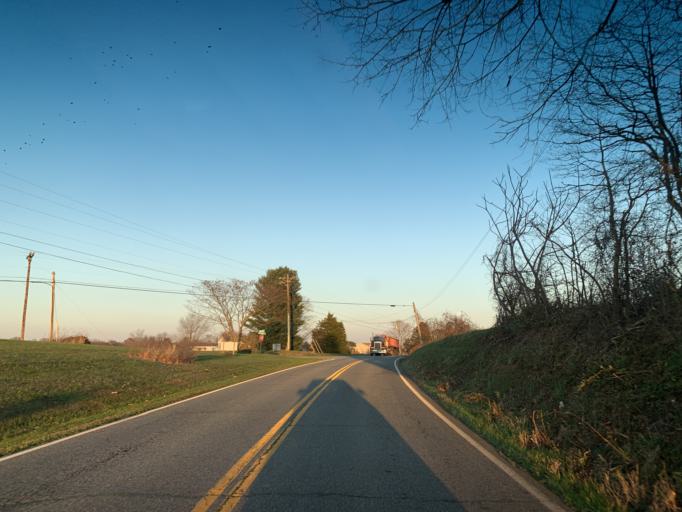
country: US
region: Maryland
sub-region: Cecil County
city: Charlestown
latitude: 39.4074
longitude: -75.9388
